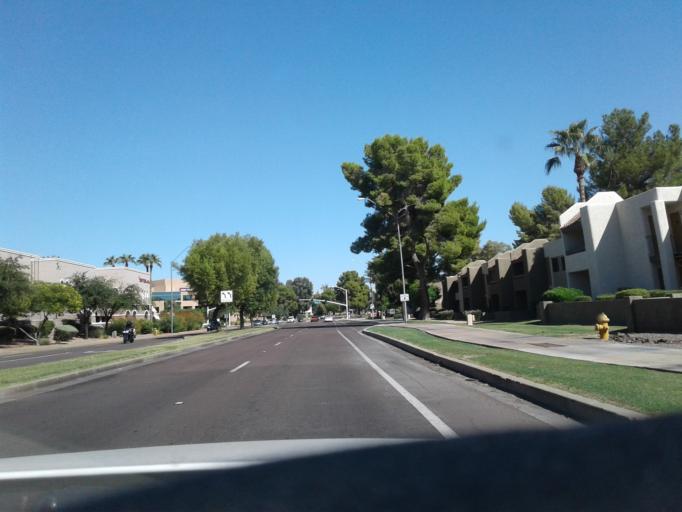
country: US
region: Arizona
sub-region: Maricopa County
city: Scottsdale
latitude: 33.5544
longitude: -111.9007
